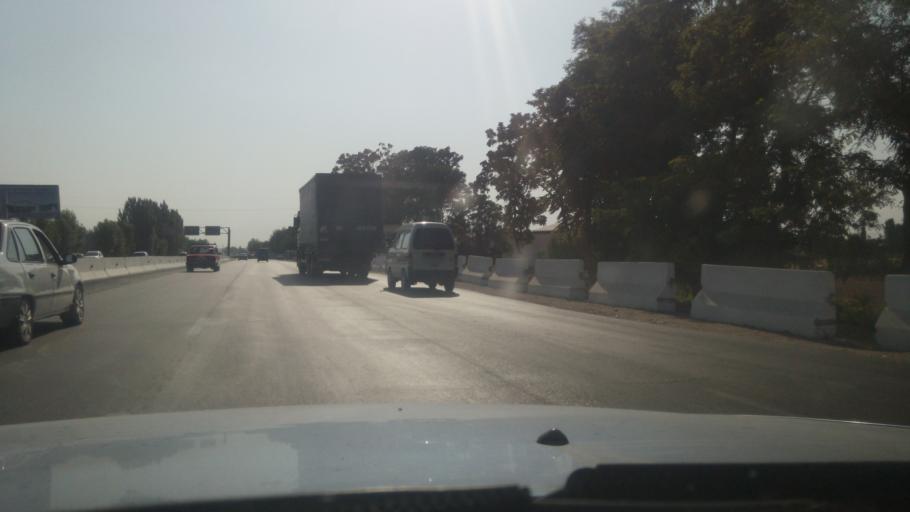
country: UZ
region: Toshkent
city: Urtaowul
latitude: 41.2210
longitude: 69.1366
